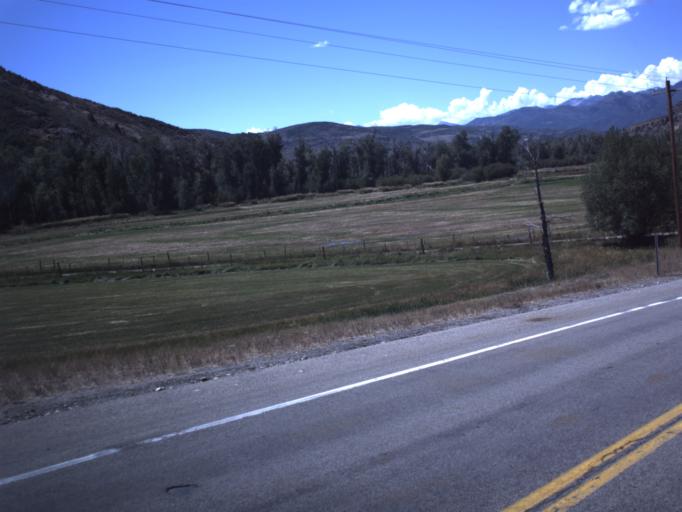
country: US
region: Utah
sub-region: Summit County
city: Francis
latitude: 40.6110
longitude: -111.2918
